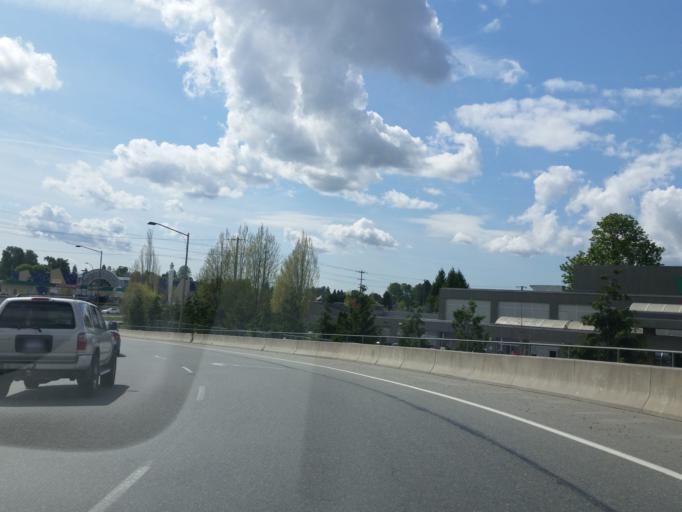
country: CA
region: British Columbia
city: Pitt Meadows
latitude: 49.2247
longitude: -122.6688
